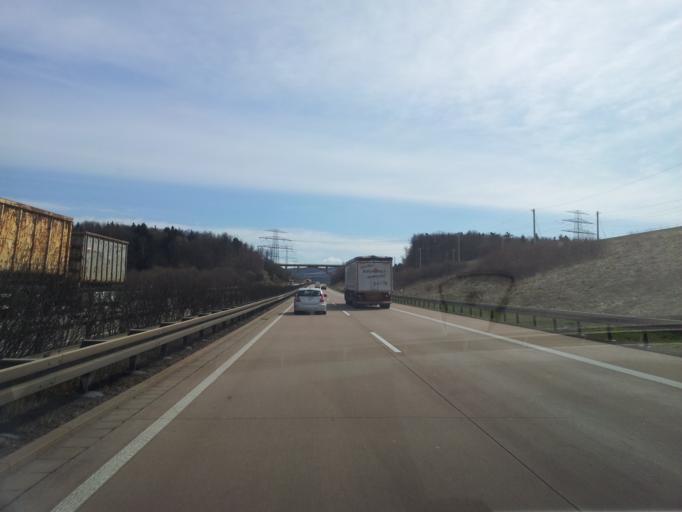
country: DE
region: Thuringia
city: Behringen
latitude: 50.7952
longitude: 11.0011
